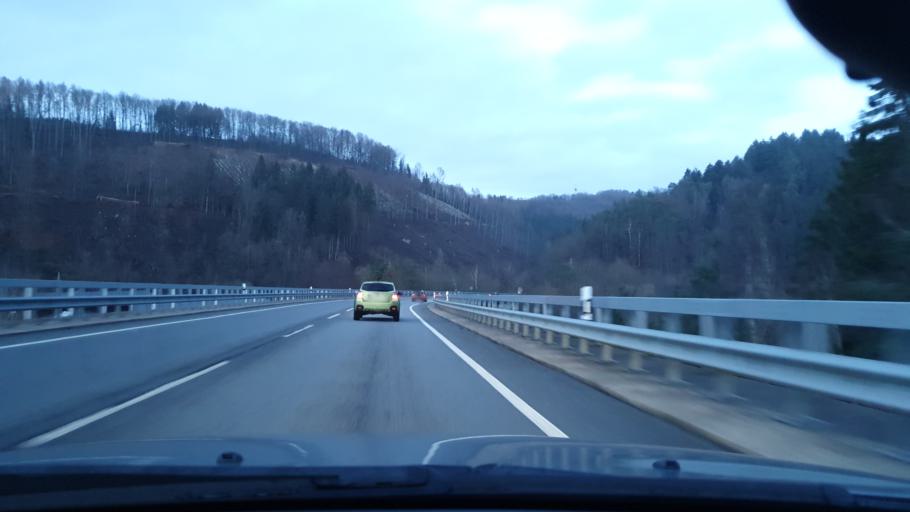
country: DE
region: Rheinland-Pfalz
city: Donsieders
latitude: 49.2659
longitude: 7.5948
